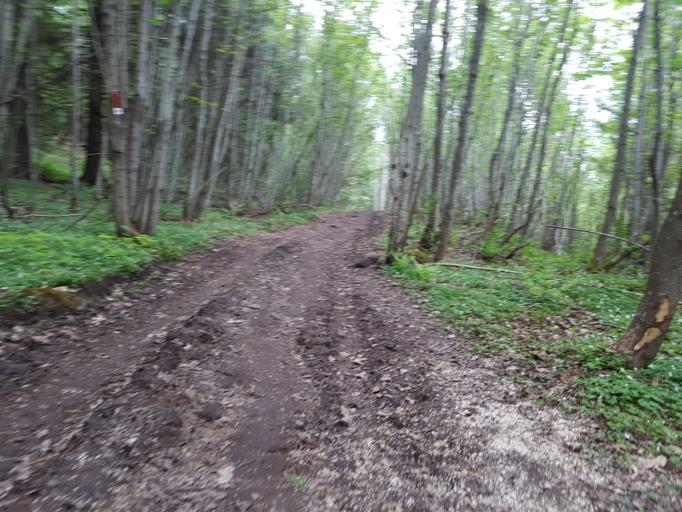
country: NO
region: Nord-Trondelag
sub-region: Levanger
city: Levanger
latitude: 63.7393
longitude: 11.2602
